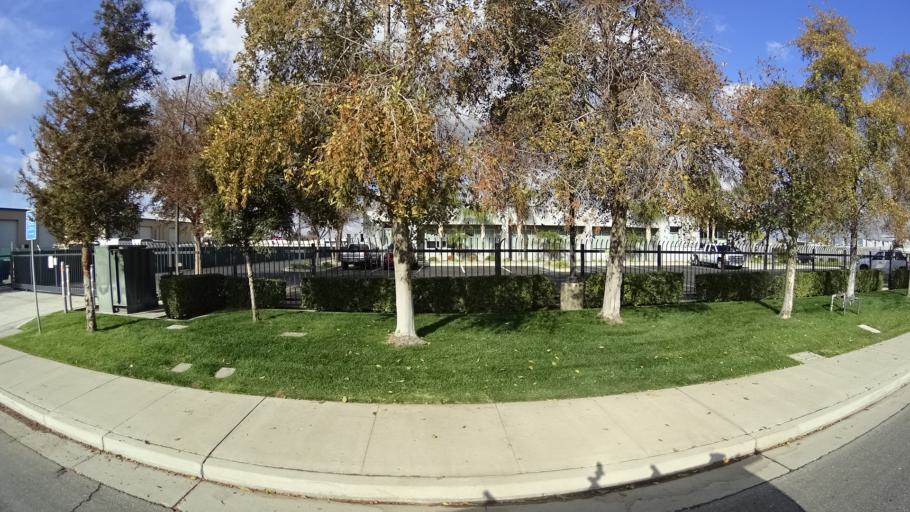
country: US
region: California
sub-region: Kern County
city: Bakersfield
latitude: 35.3469
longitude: -118.9709
